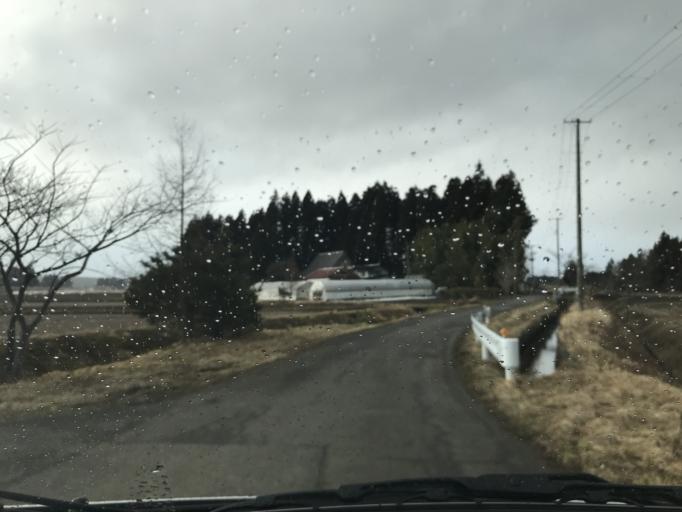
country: JP
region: Iwate
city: Mizusawa
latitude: 39.0824
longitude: 141.0415
